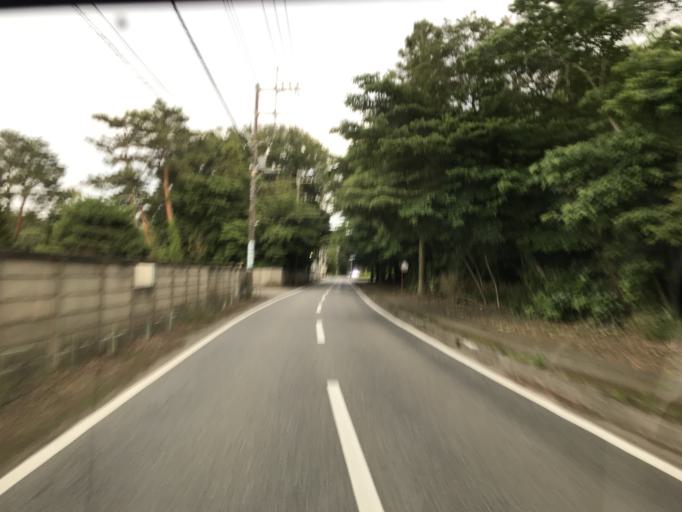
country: JP
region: Chiba
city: Noda
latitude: 35.9585
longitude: 139.8928
